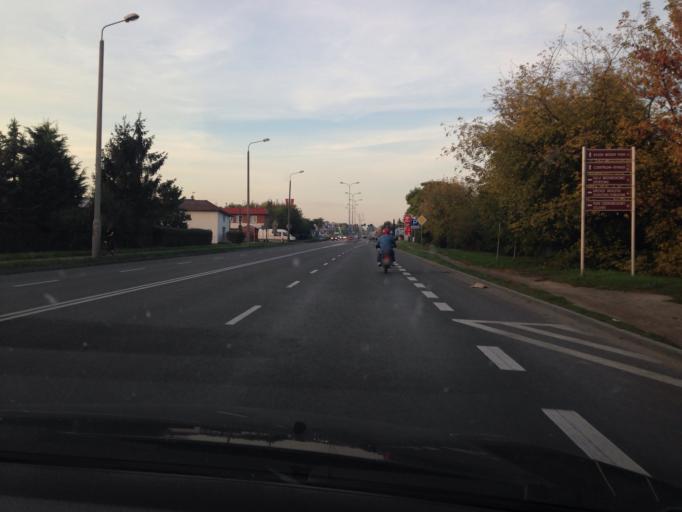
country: PL
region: Kujawsko-Pomorskie
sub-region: Powiat inowroclawski
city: Inowroclaw
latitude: 52.7765
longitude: 18.2595
